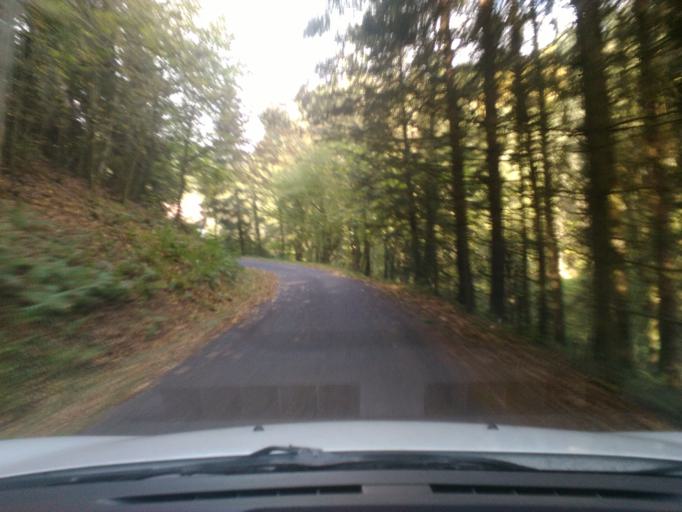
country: FR
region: Lorraine
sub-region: Departement des Vosges
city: Ban-de-Laveline
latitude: 48.2984
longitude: 7.0595
